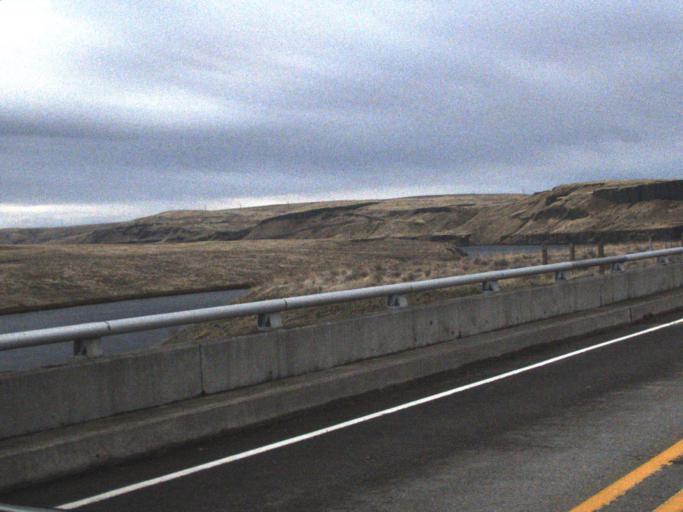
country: US
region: Washington
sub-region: Walla Walla County
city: Waitsburg
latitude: 46.5643
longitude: -118.1865
